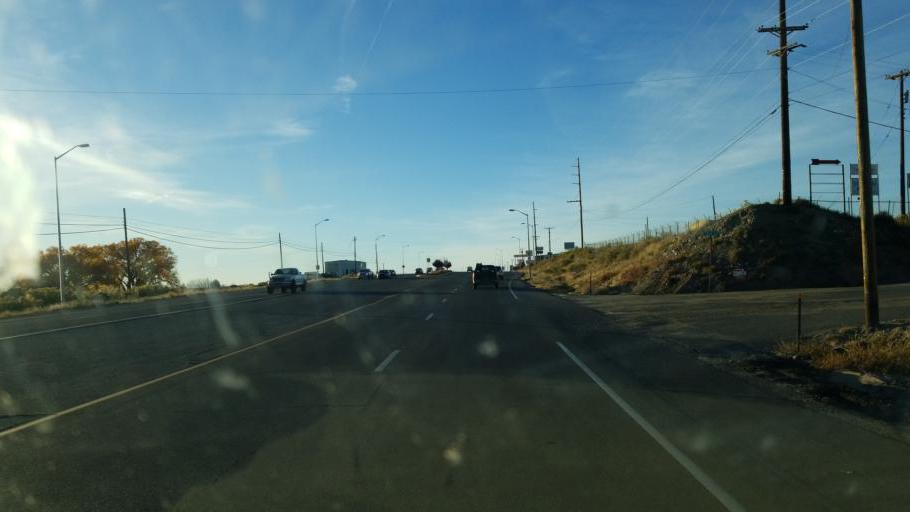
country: US
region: New Mexico
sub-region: San Juan County
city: Farmington
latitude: 36.7157
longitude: -108.1508
